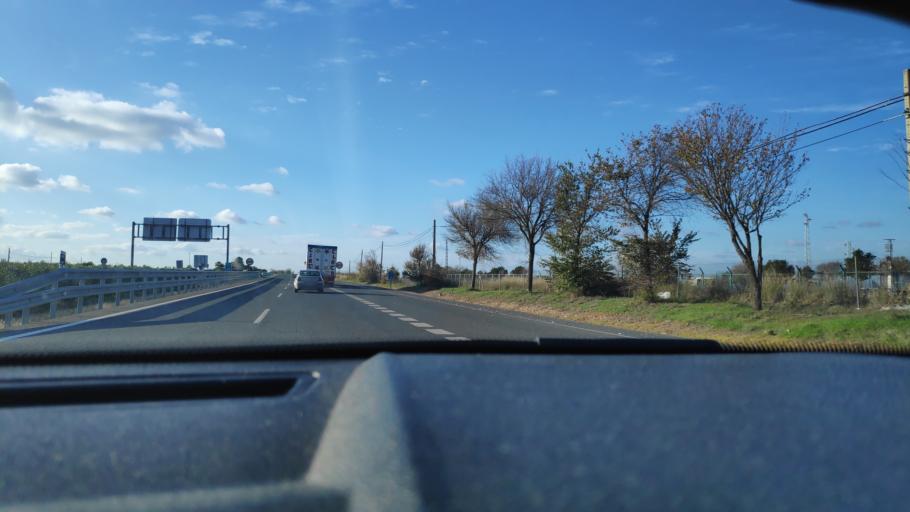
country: ES
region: Andalusia
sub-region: Provincia de Sevilla
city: La Luisiana
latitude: 37.5268
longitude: -5.2630
